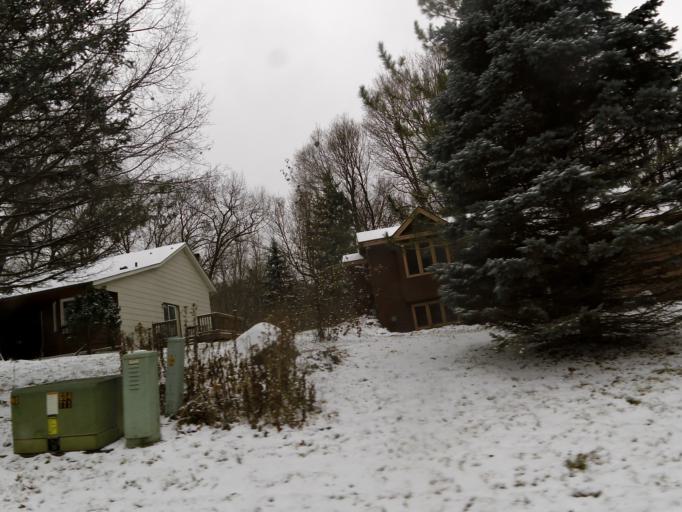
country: US
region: Minnesota
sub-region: Scott County
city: Prior Lake
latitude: 44.7005
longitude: -93.4550
